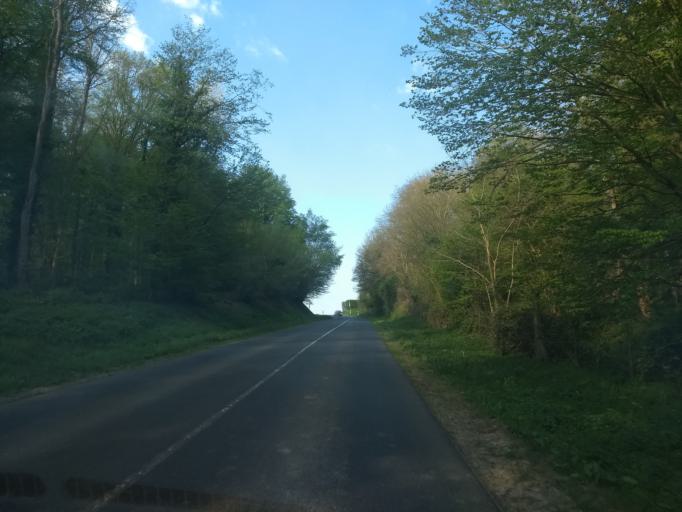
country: FR
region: Picardie
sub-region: Departement de la Somme
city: Poulainville
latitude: 49.9674
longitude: 2.4002
